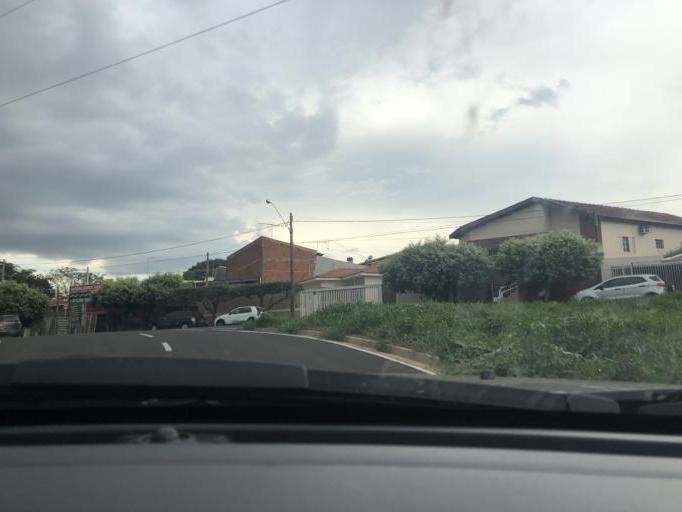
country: BR
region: Sao Paulo
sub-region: Sao Jose Do Rio Preto
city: Sao Jose do Rio Preto
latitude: -20.8442
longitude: -49.3831
